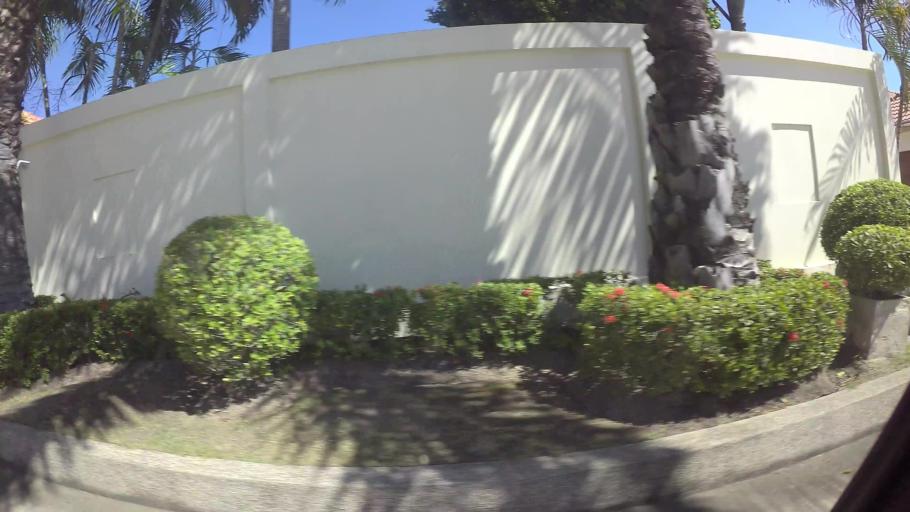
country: TH
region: Chon Buri
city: Phatthaya
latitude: 12.9166
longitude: 100.8590
